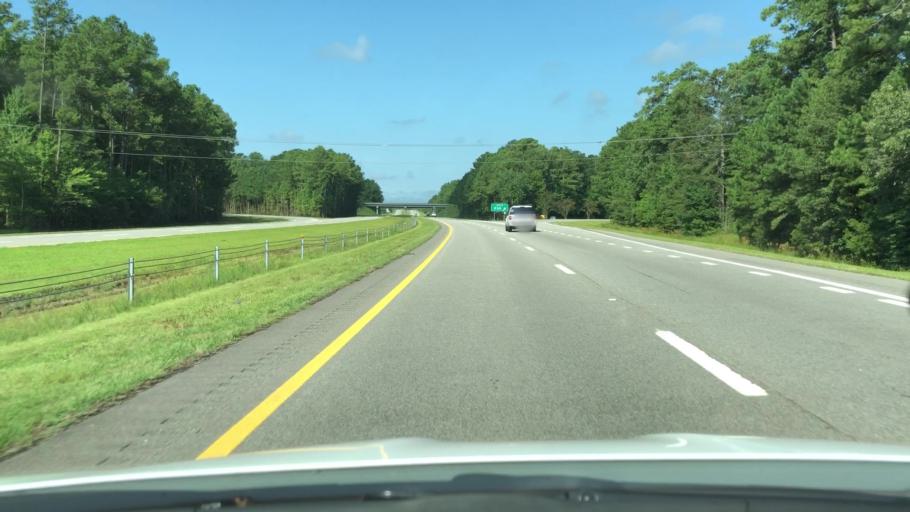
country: US
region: North Carolina
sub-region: Chowan County
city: Edenton
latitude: 36.0931
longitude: -76.5663
